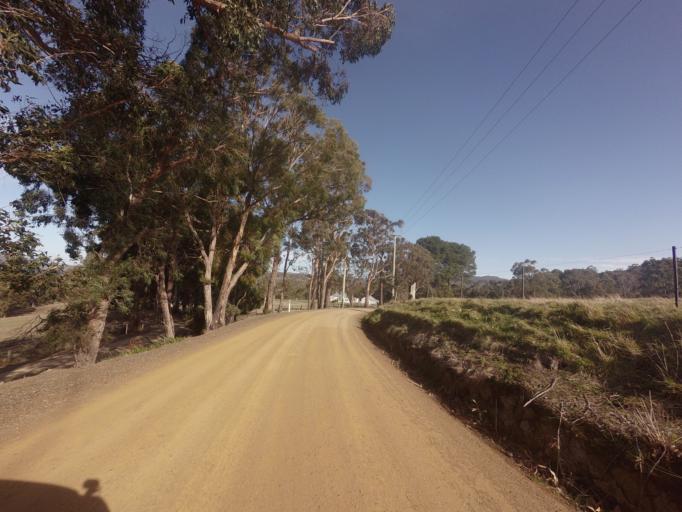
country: AU
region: Tasmania
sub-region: Kingborough
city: Kettering
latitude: -43.1007
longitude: 147.2638
